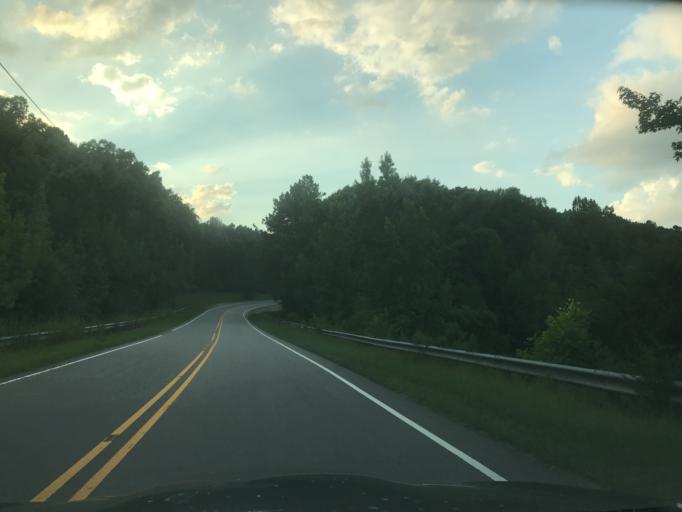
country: US
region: North Carolina
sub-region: Wake County
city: Wake Forest
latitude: 35.9293
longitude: -78.6064
